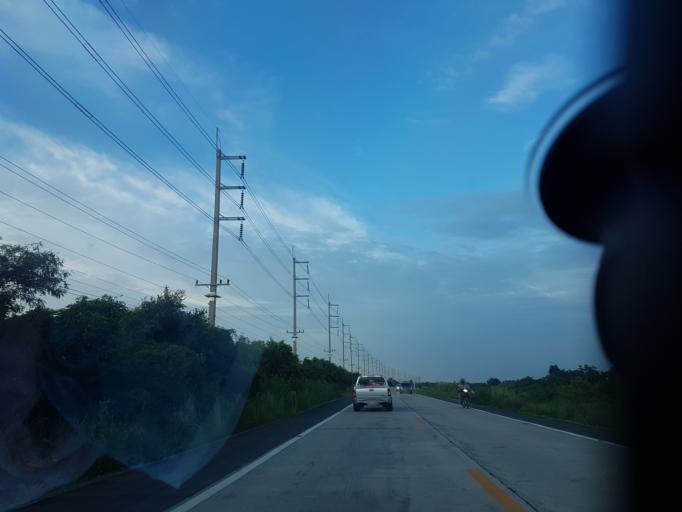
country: TH
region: Phra Nakhon Si Ayutthaya
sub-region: Amphoe Tha Ruea
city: Tha Ruea
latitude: 14.5350
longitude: 100.7486
